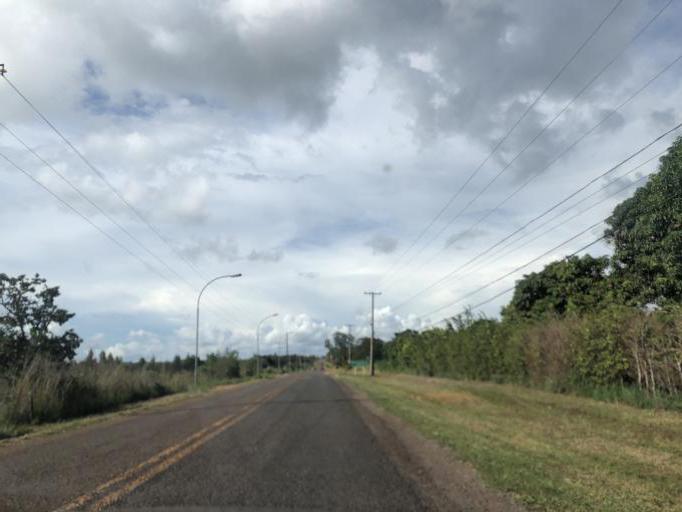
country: BR
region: Federal District
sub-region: Brasilia
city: Brasilia
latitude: -15.7458
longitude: -48.1260
